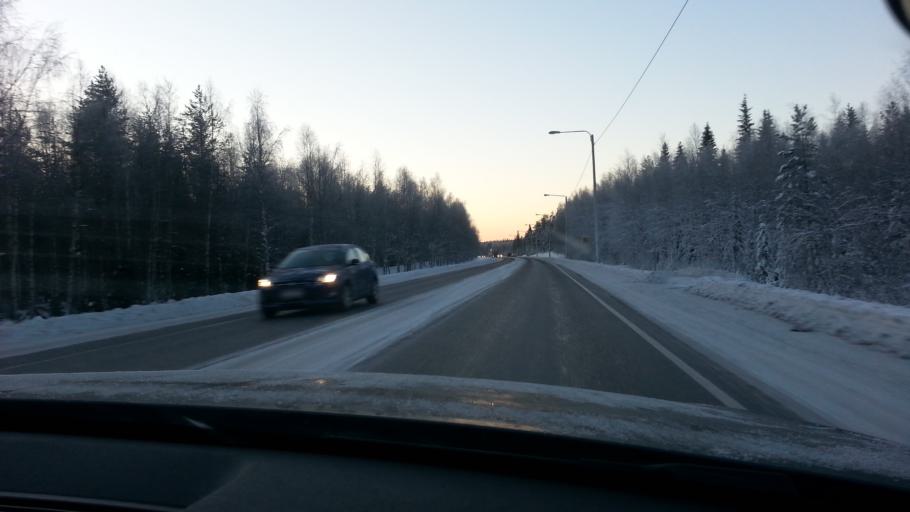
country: FI
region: Lapland
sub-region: Rovaniemi
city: Rovaniemi
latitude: 66.5333
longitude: 25.7708
